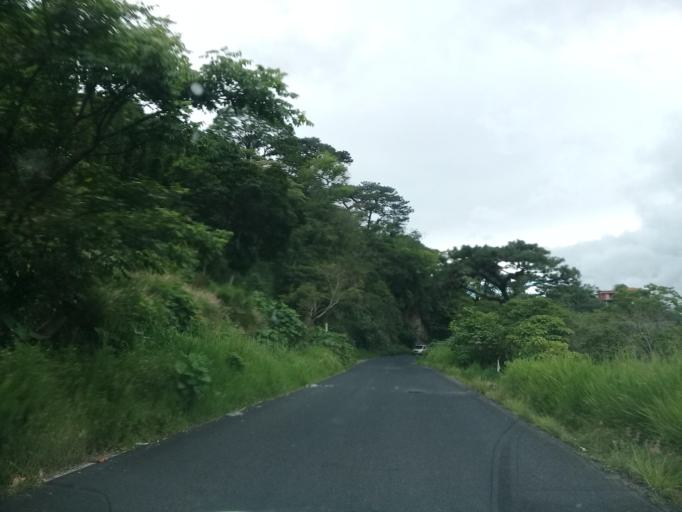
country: MX
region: Veracruz
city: El Castillo
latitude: 19.5610
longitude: -96.8477
